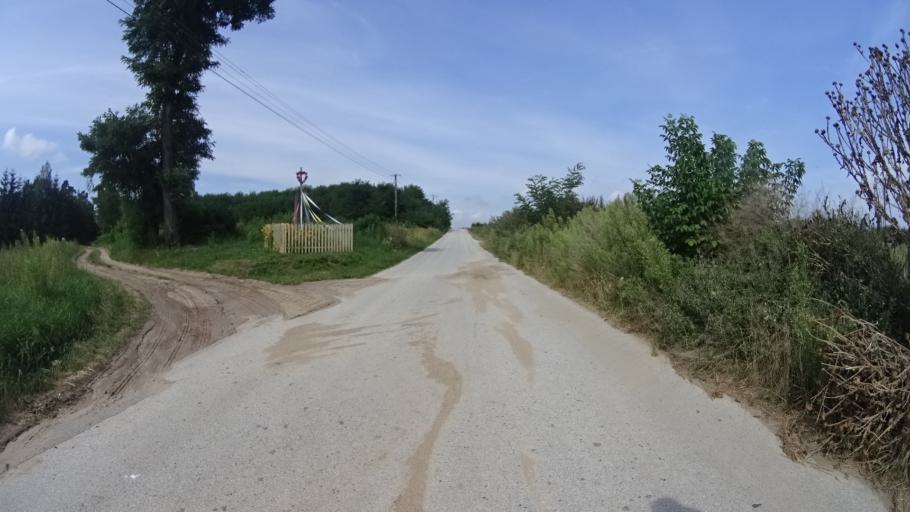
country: PL
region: Masovian Voivodeship
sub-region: Powiat grojecki
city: Goszczyn
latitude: 51.6845
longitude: 20.8420
